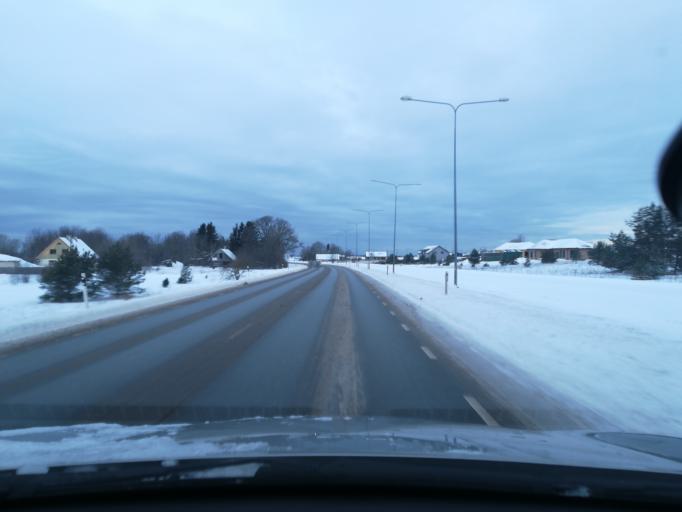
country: EE
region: Harju
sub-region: Harku vald
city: Tabasalu
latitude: 59.4405
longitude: 24.4954
